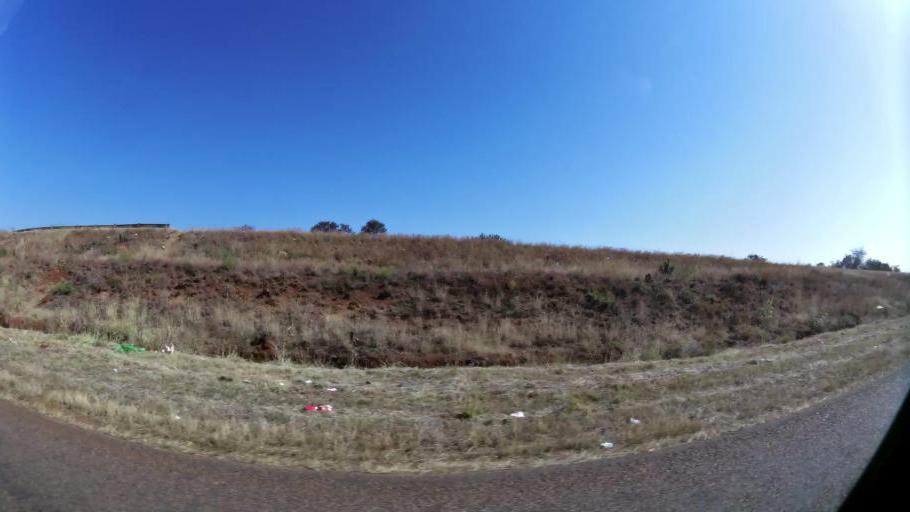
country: ZA
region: North-West
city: Ga-Rankuwa
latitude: -25.6273
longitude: 28.1107
